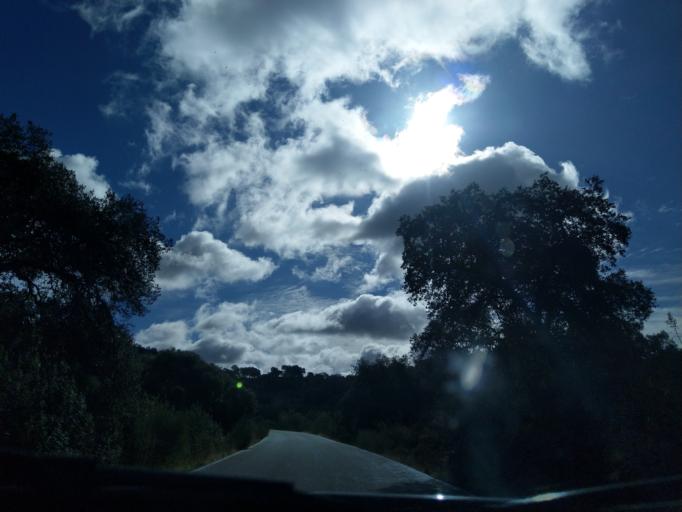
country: ES
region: Extremadura
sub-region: Provincia de Badajoz
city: Reina
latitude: 38.1325
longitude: -5.9178
